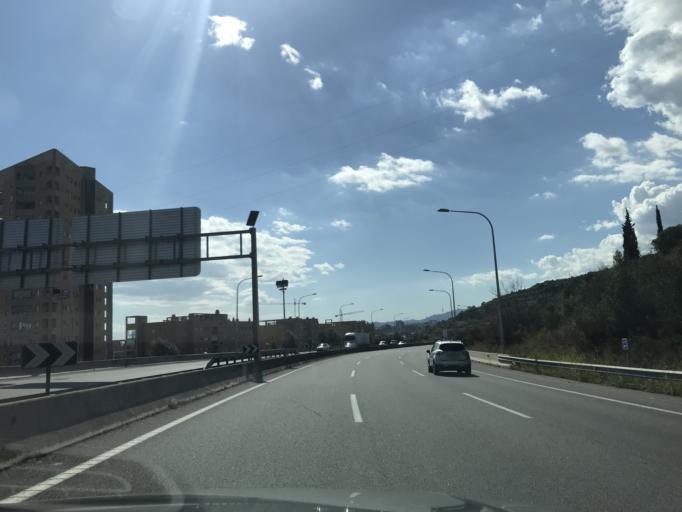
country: ES
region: Catalonia
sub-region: Provincia de Barcelona
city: Montgat
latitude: 41.4662
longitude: 2.2759
